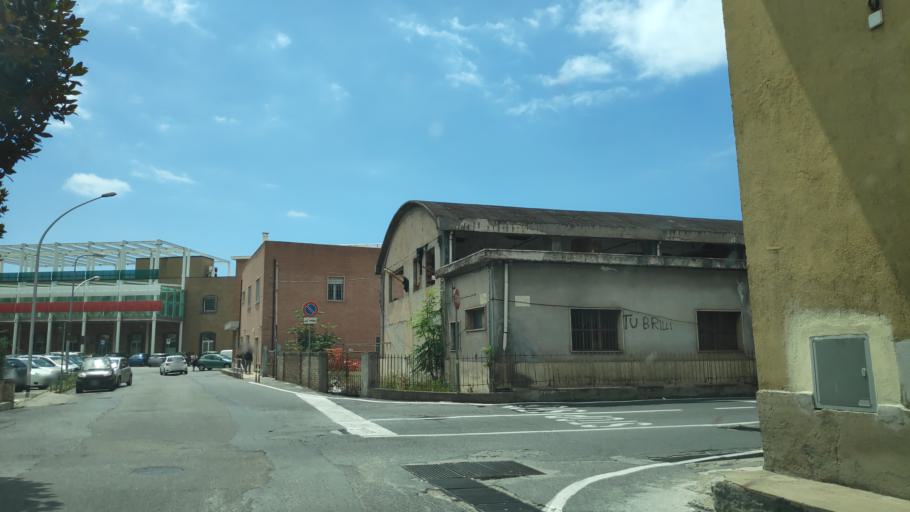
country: IT
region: Calabria
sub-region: Provincia di Cosenza
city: Paola
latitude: 39.3604
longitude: 16.0336
